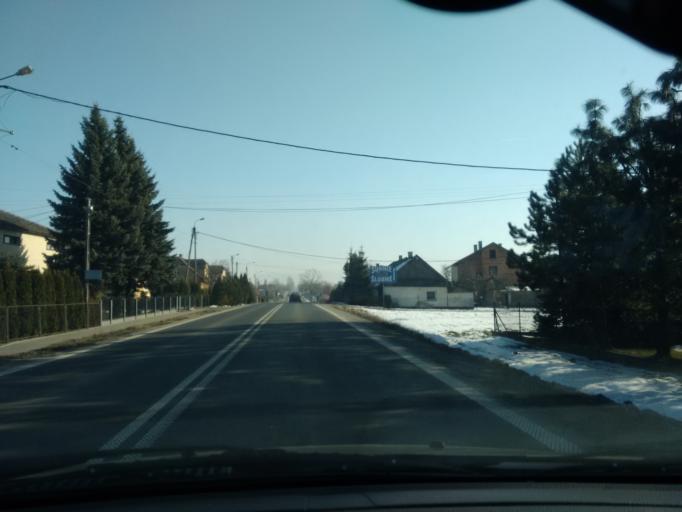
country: PL
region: Lesser Poland Voivodeship
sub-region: Powiat oswiecimski
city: Bulowice
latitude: 49.8696
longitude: 19.3044
